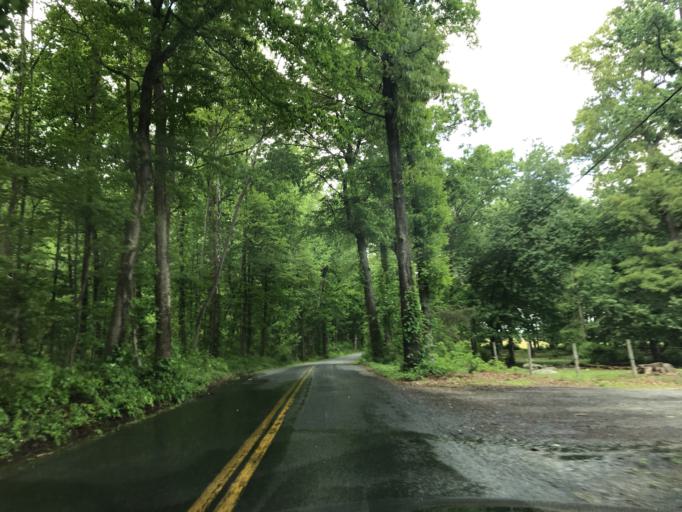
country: US
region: Pennsylvania
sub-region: York County
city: Susquehanna Trails
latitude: 39.7098
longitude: -76.3247
